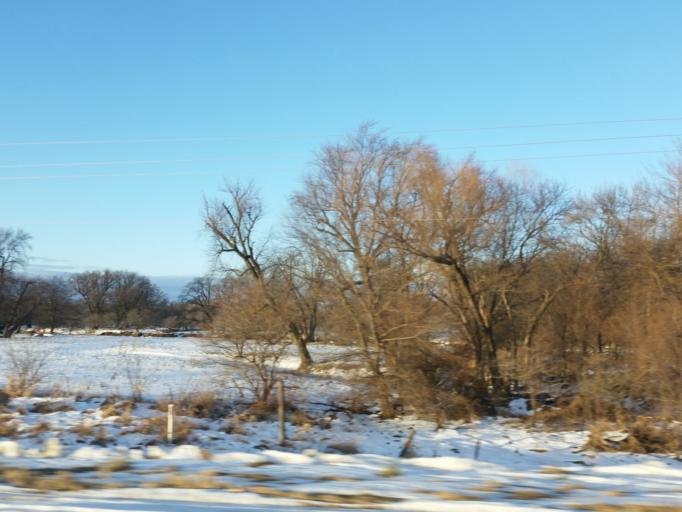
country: US
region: Iowa
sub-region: Butler County
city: Aplington
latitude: 42.7451
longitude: -92.9907
